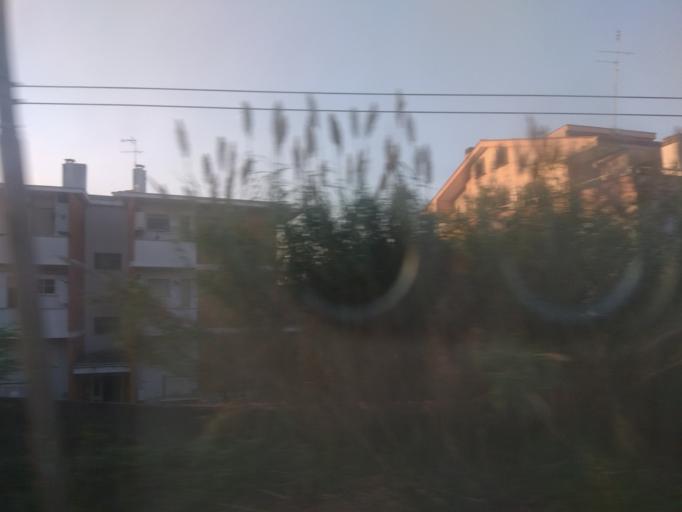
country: IT
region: Latium
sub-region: Citta metropolitana di Roma Capitale
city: Santa Marinella
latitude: 42.0343
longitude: 11.8498
